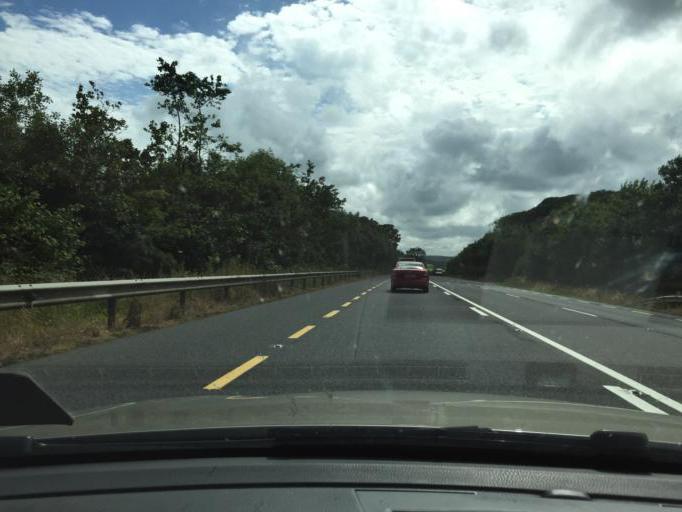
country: IE
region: Munster
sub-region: Waterford
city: Portlaw
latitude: 52.2072
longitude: -7.4002
